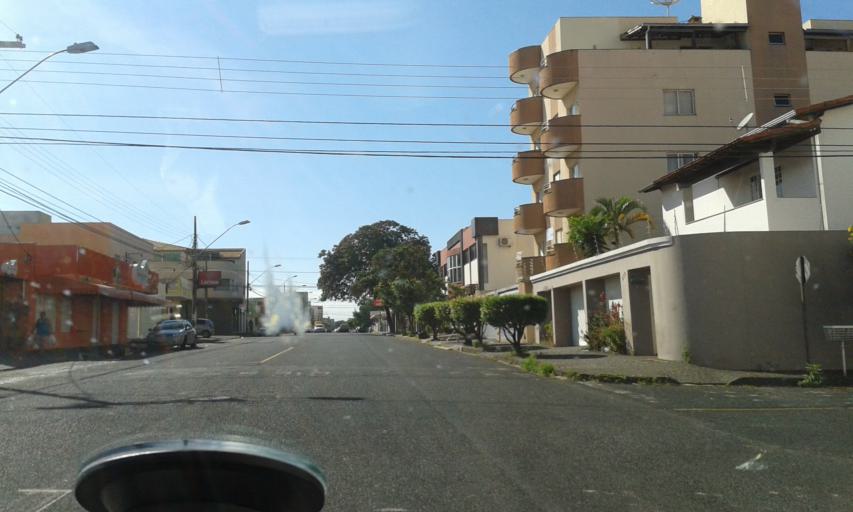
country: BR
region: Minas Gerais
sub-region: Uberlandia
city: Uberlandia
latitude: -18.9229
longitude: -48.2462
